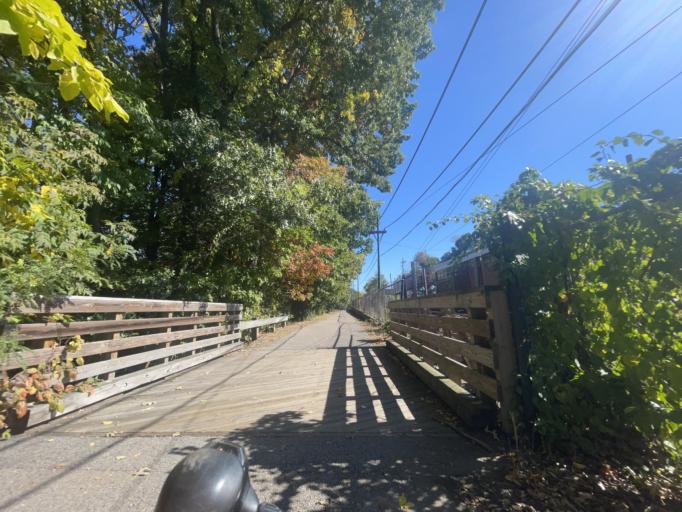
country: US
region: Massachusetts
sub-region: Norfolk County
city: Milton
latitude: 42.2702
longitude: -71.0729
